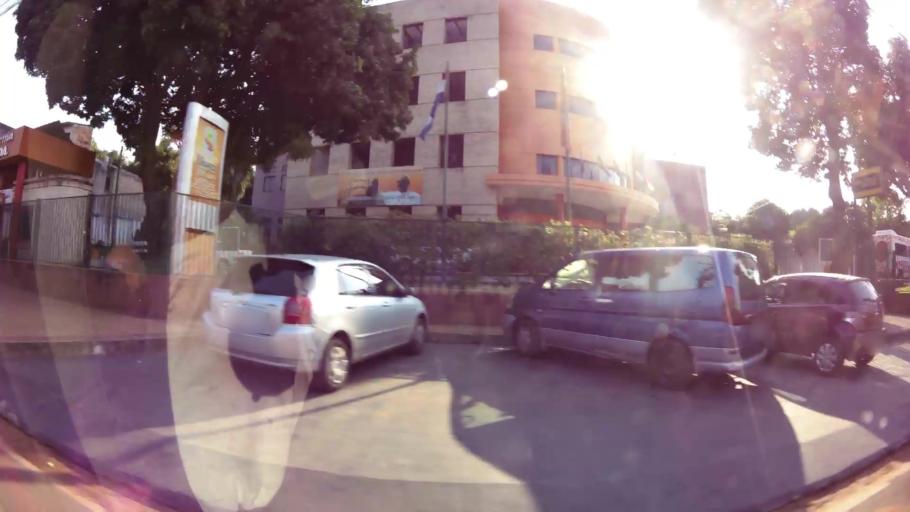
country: PY
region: Central
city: Lambare
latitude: -25.3434
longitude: -57.5917
